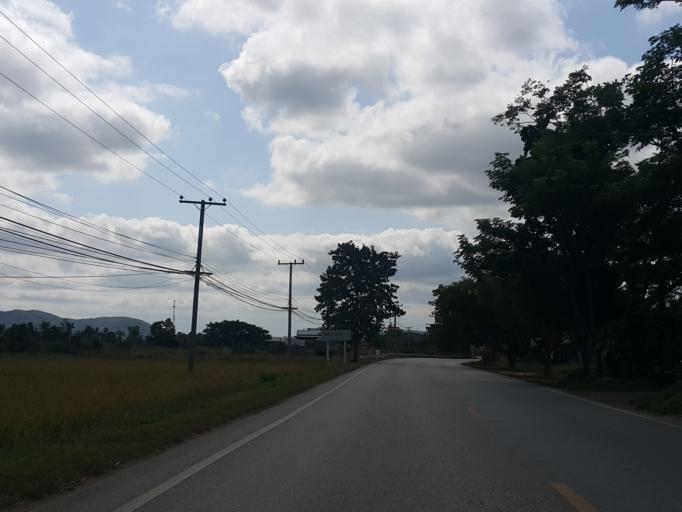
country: TH
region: Lamphun
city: Ban Thi
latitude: 18.6634
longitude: 99.1328
